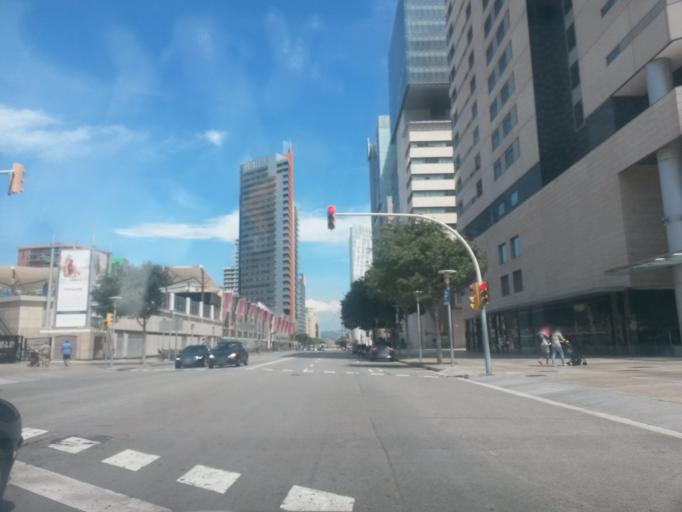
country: ES
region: Catalonia
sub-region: Provincia de Barcelona
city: Sant Marti
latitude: 41.4086
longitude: 2.2169
